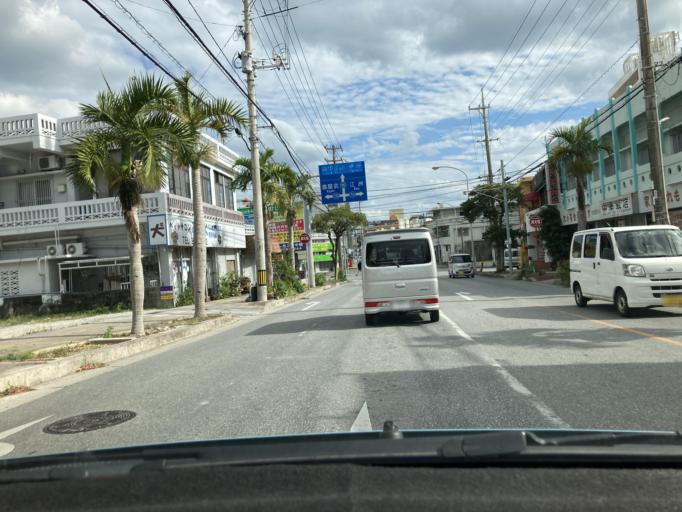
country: JP
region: Okinawa
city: Okinawa
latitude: 26.3558
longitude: 127.8314
